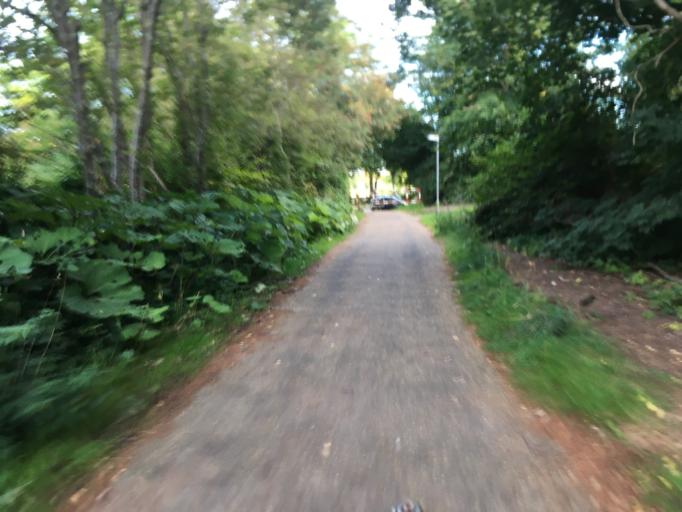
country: DK
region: Capital Region
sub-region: Hillerod Kommune
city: Hillerod
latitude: 55.9230
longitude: 12.3001
